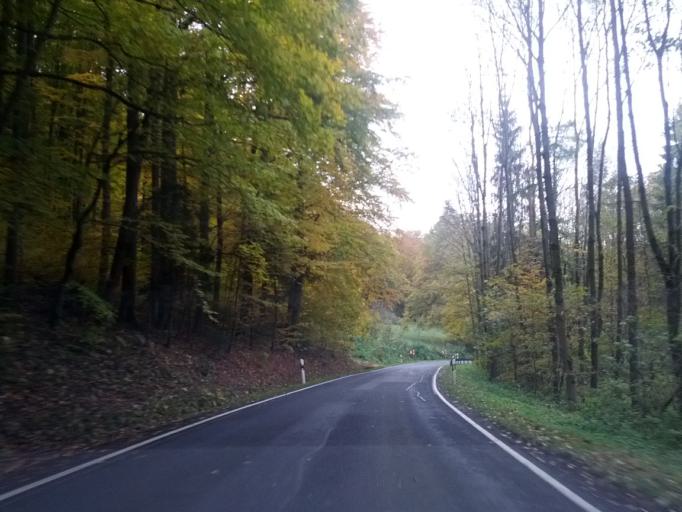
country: DE
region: Thuringia
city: Frankenroda
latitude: 51.1228
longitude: 10.2971
